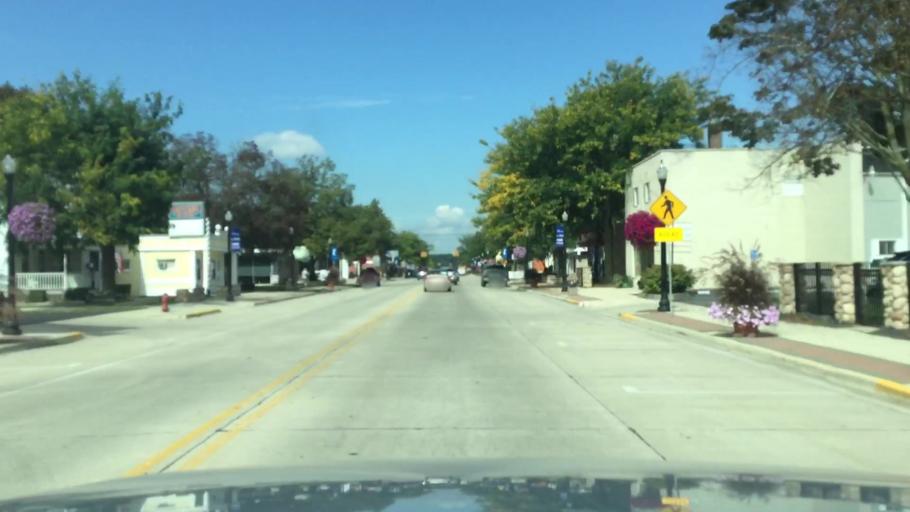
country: US
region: Michigan
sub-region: Wayne County
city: Belleville
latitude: 42.2059
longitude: -83.4869
